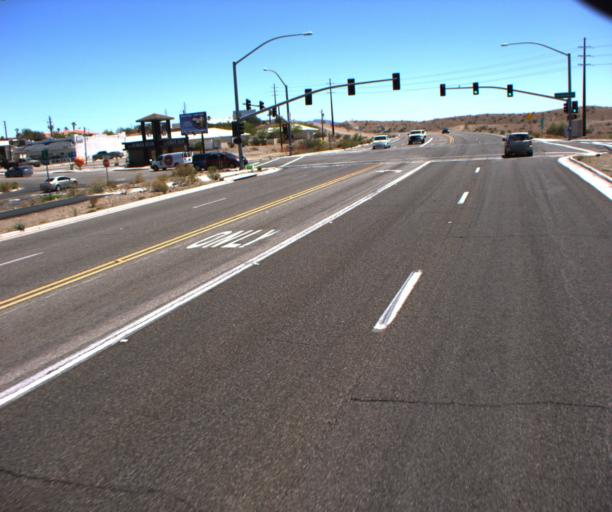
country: US
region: Arizona
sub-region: Mohave County
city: Lake Havasu City
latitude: 34.4531
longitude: -114.2663
